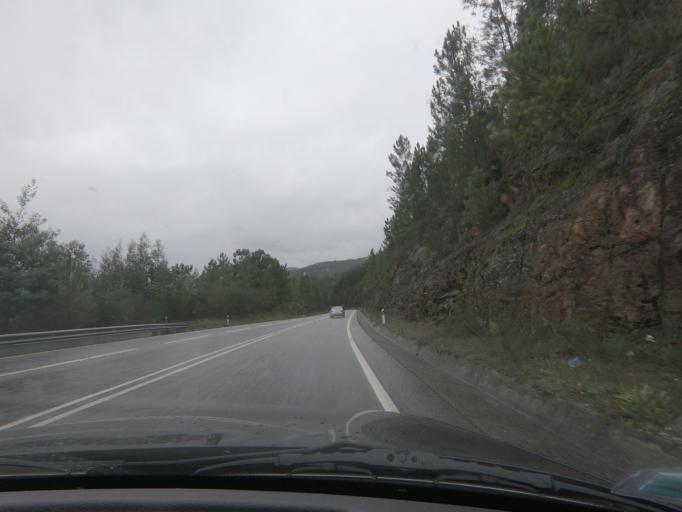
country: PT
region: Porto
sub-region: Amarante
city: Teloes
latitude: 41.3242
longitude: -8.0576
